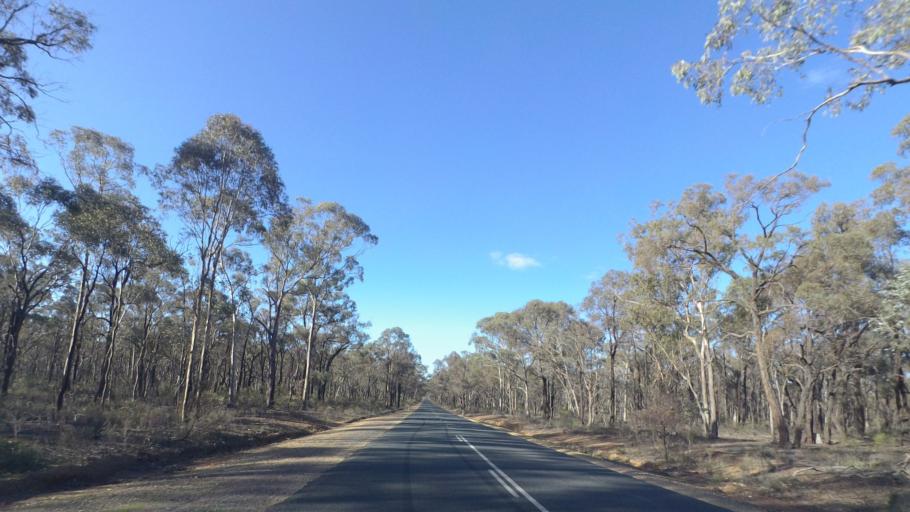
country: AU
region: Victoria
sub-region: Greater Bendigo
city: Epsom
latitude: -36.6643
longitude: 144.4445
